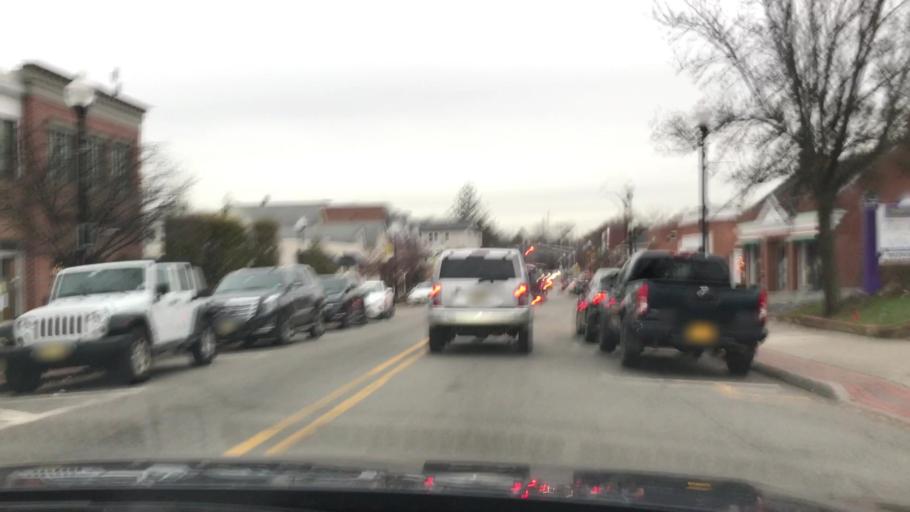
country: US
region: New Jersey
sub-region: Bergen County
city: Ridgewood
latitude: 40.9789
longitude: -74.1149
